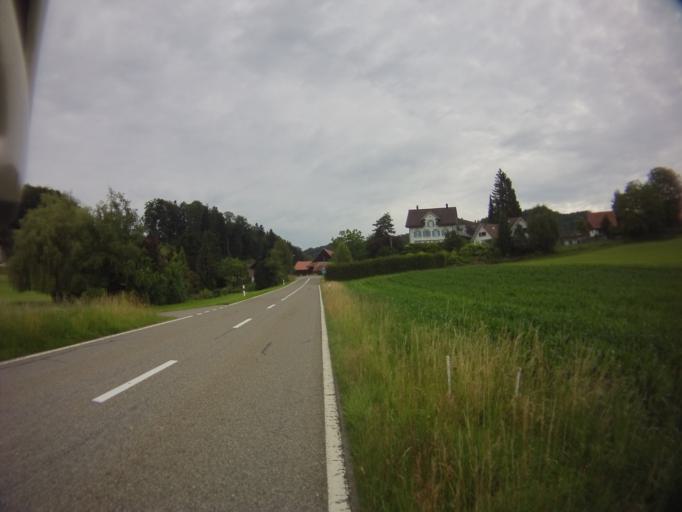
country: CH
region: Zurich
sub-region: Bezirk Affoltern
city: Hausen am Albis / Hausen (Dorf)
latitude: 47.2582
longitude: 8.5106
